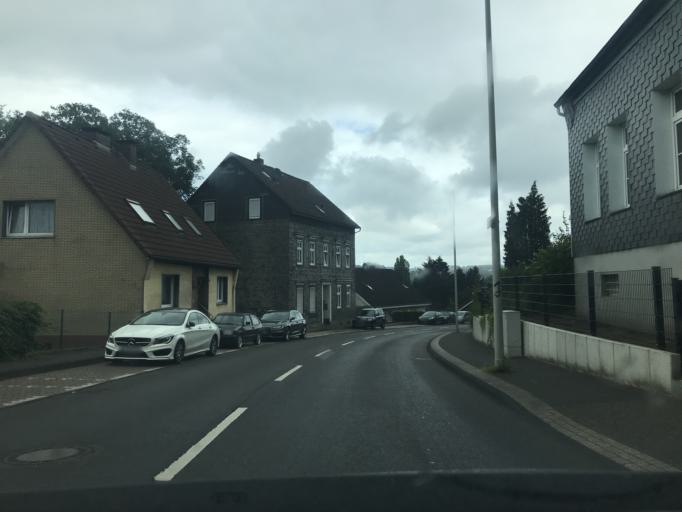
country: DE
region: North Rhine-Westphalia
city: Haan
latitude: 51.1948
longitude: 7.0472
